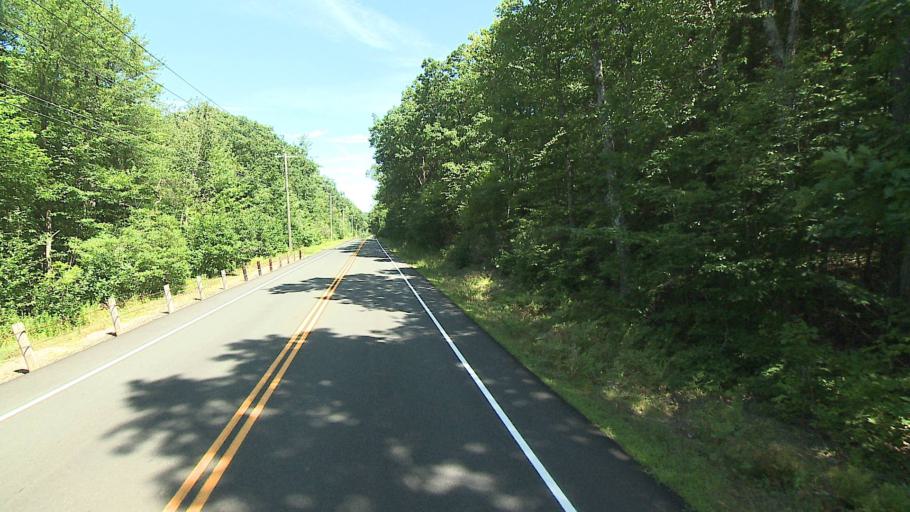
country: US
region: Connecticut
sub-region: Hartford County
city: North Granby
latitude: 41.9766
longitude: -72.9155
